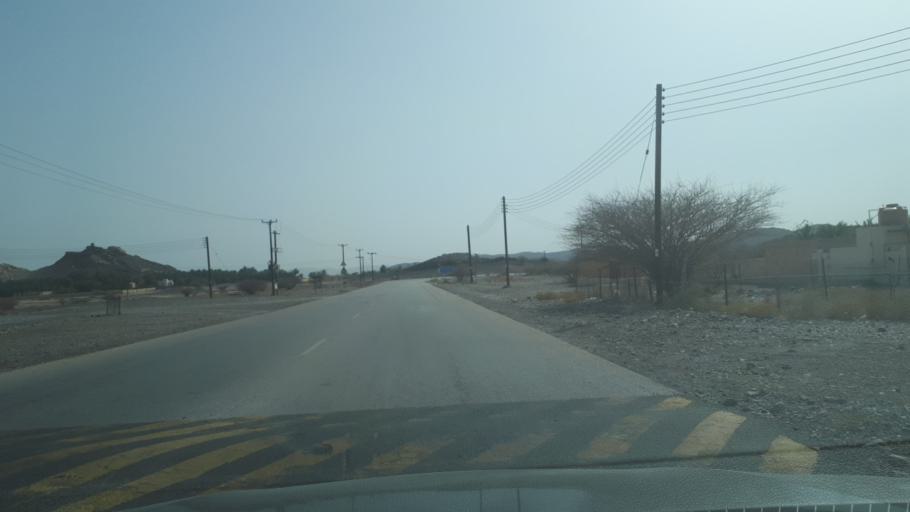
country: OM
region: Az Zahirah
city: `Ibri
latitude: 23.1475
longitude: 56.9036
